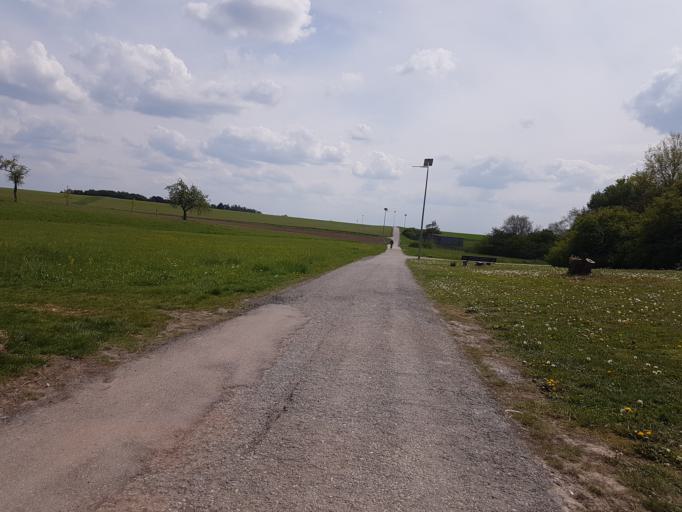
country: DE
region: Baden-Wuerttemberg
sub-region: Regierungsbezirk Stuttgart
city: Herrenberg
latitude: 48.5877
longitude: 8.8778
